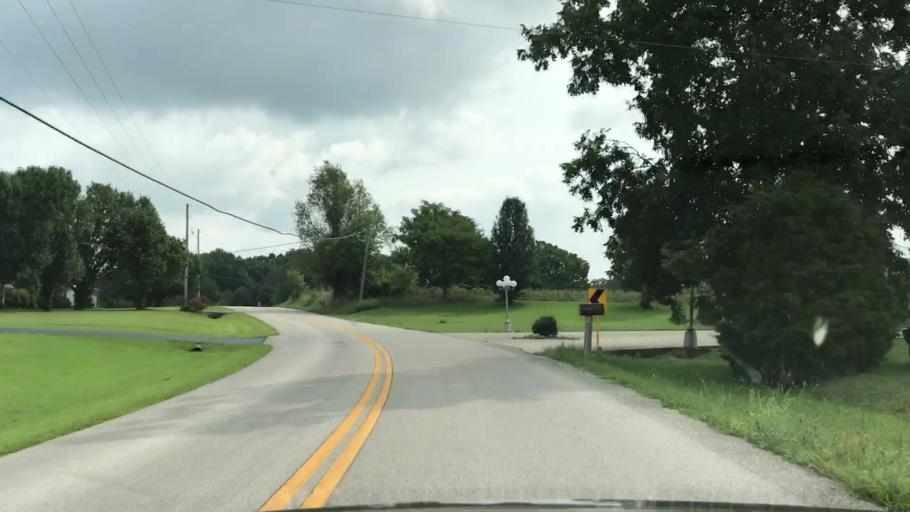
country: US
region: Kentucky
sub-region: Edmonson County
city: Brownsville
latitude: 37.1559
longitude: -86.2171
